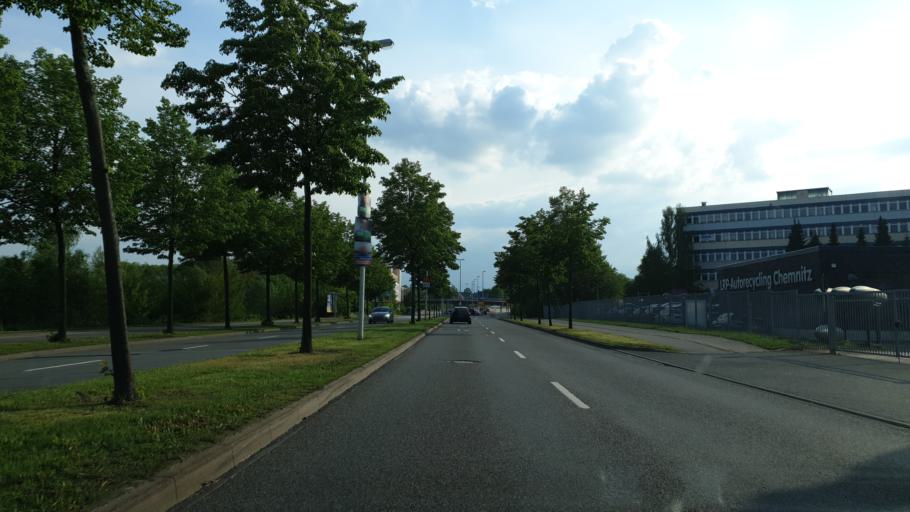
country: DE
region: Saxony
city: Neukirchen
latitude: 50.8145
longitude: 12.8787
